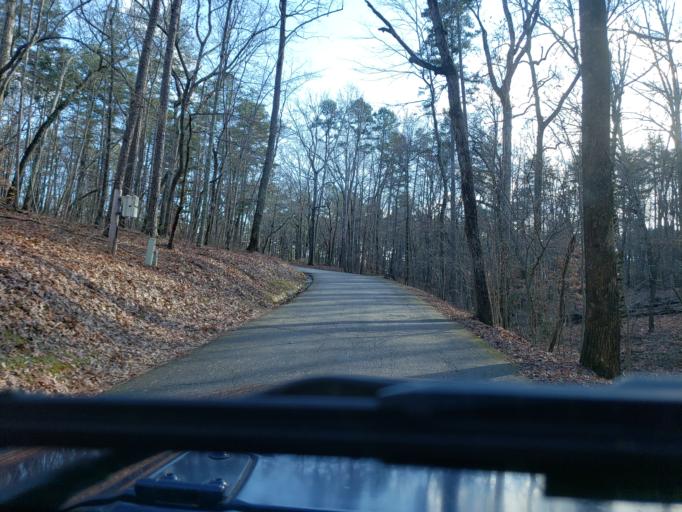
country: US
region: North Carolina
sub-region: Cleveland County
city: Kings Mountain
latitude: 35.1496
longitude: -81.3355
